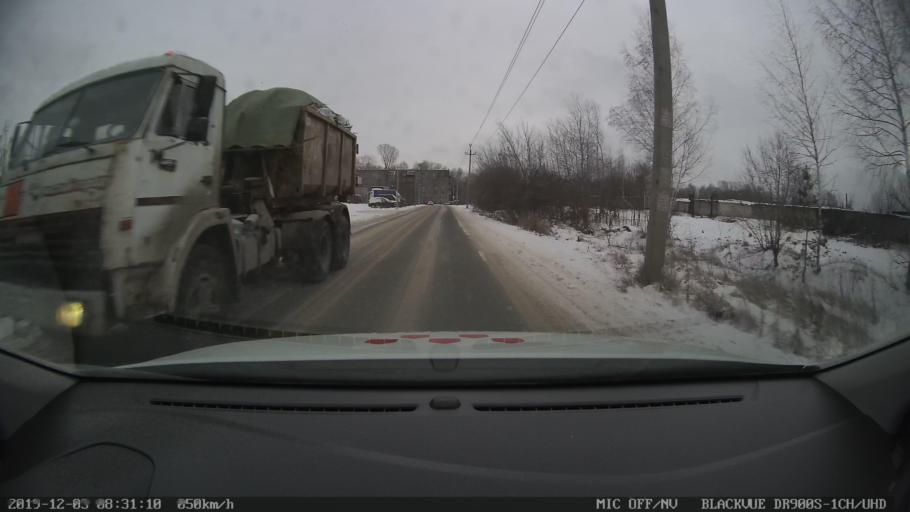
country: RU
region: Tatarstan
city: Staroye Arakchino
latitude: 55.8773
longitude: 49.0109
